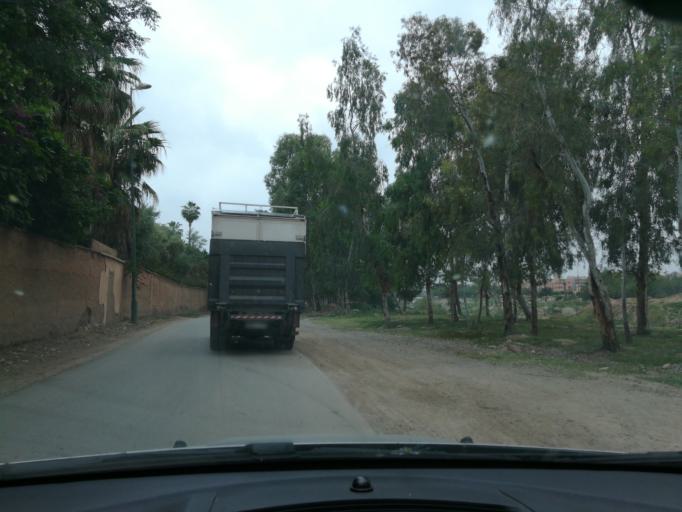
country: MA
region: Marrakech-Tensift-Al Haouz
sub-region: Marrakech
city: Marrakesh
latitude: 31.6591
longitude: -7.9834
